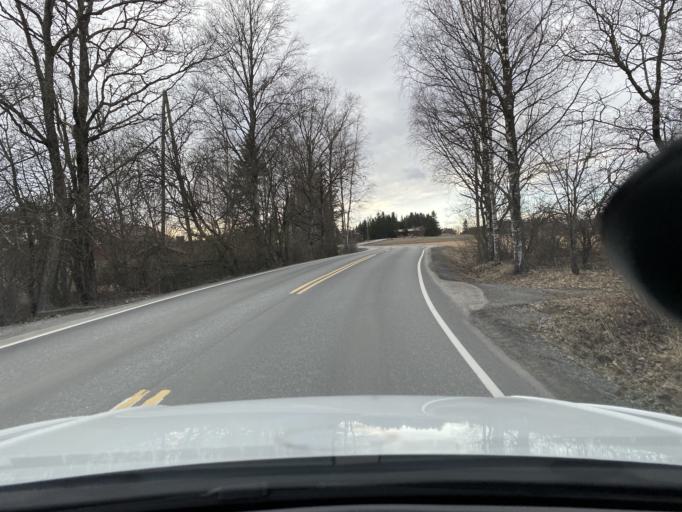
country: FI
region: Pirkanmaa
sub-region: Tampere
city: Vesilahti
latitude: 61.2885
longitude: 23.6123
